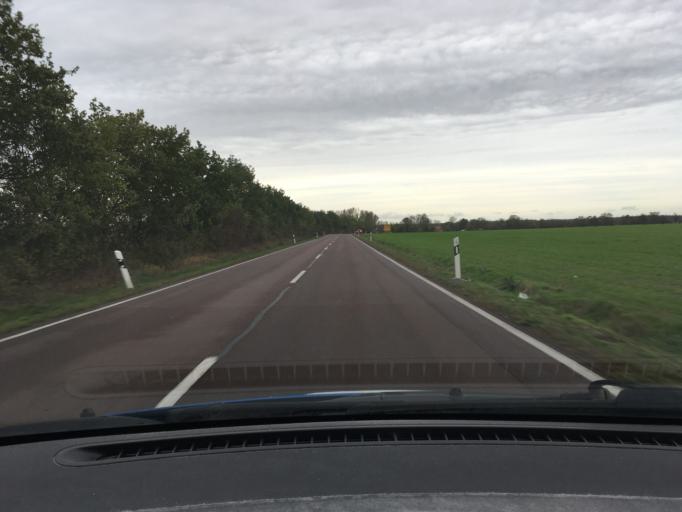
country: DE
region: Saxony-Anhalt
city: Zerbst
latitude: 52.0110
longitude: 12.0197
